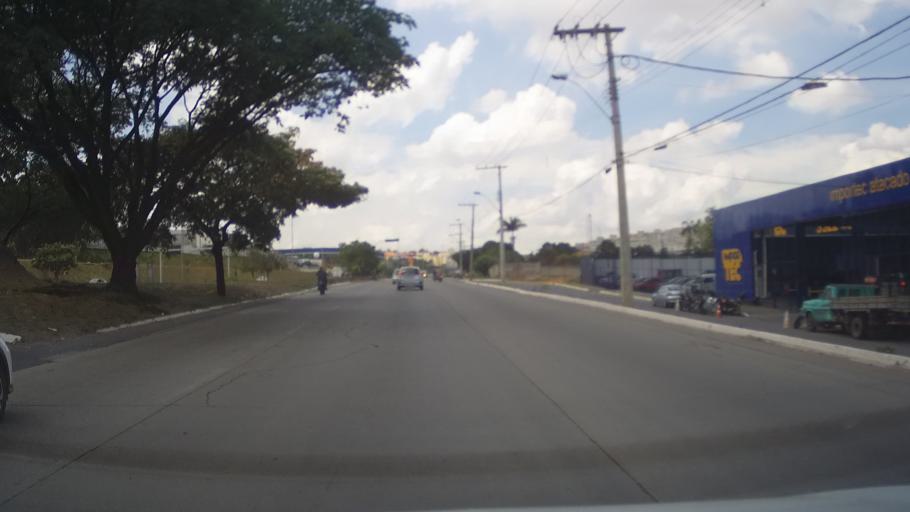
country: BR
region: Minas Gerais
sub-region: Contagem
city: Contagem
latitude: -19.9370
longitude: -44.0257
